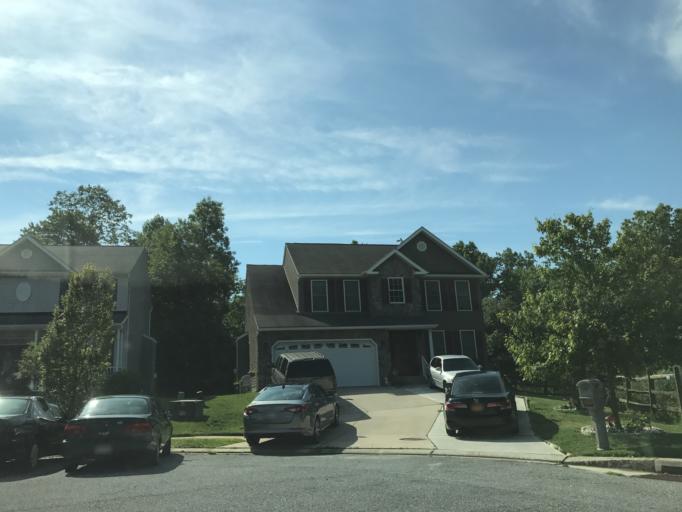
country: US
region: Maryland
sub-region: Baltimore County
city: Rossville
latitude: 39.3497
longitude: -76.4914
